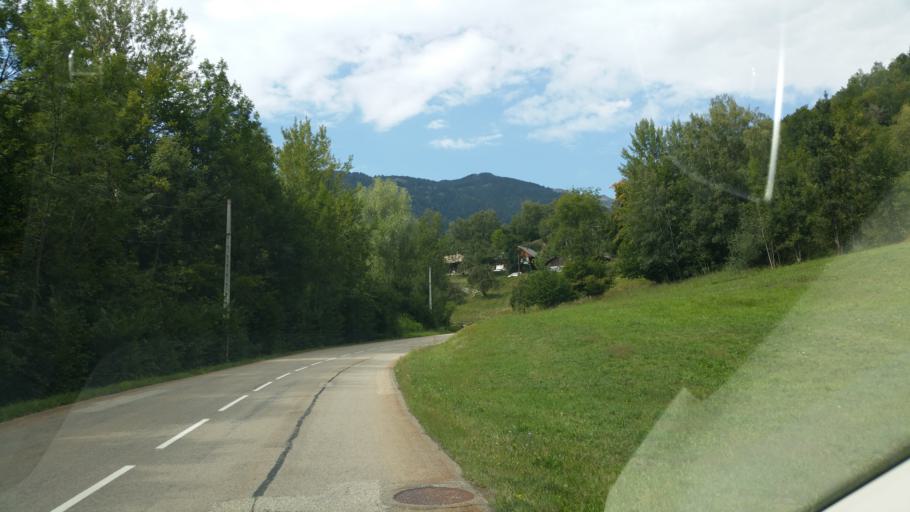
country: FR
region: Rhone-Alpes
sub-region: Departement de la Savoie
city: La Chambre
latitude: 45.3827
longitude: 6.3293
